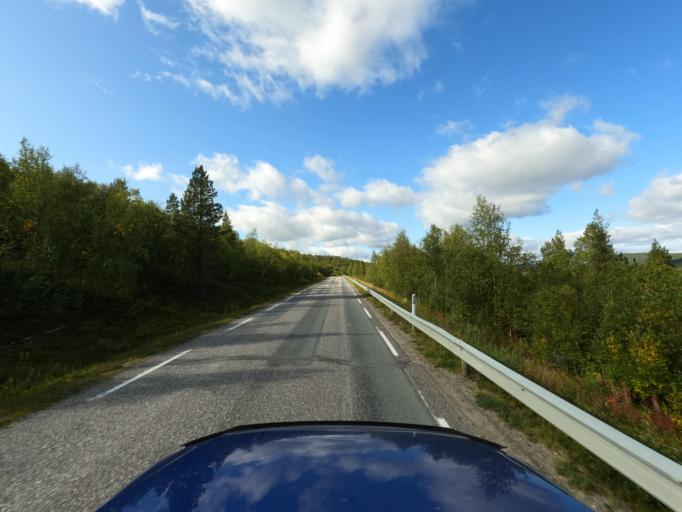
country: NO
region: Finnmark Fylke
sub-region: Karasjok
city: Karasjohka
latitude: 69.4360
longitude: 25.6829
